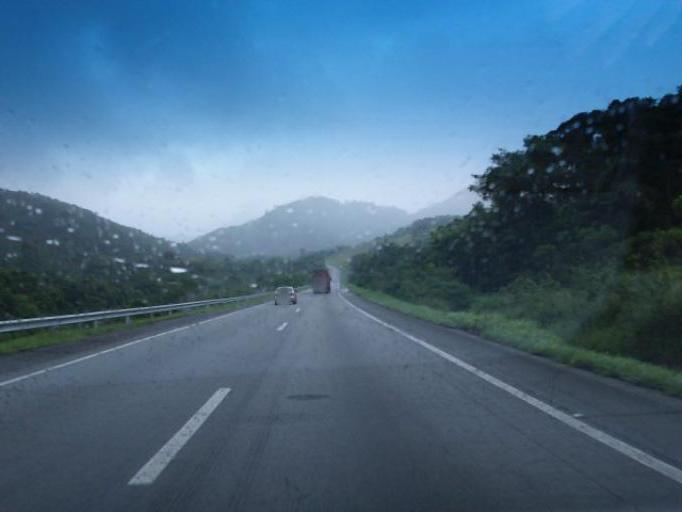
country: BR
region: Sao Paulo
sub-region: Cajati
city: Cajati
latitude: -24.8957
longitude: -48.2407
